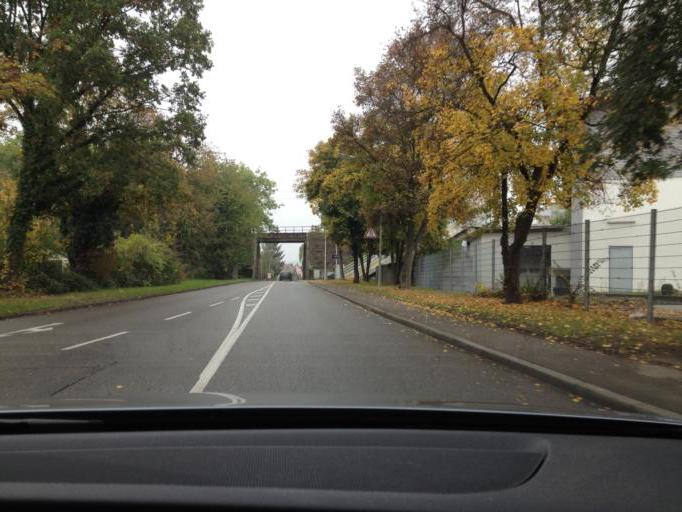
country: DE
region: Baden-Wuerttemberg
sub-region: Regierungsbezirk Stuttgart
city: Untereisesheim
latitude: 49.2291
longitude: 9.1880
